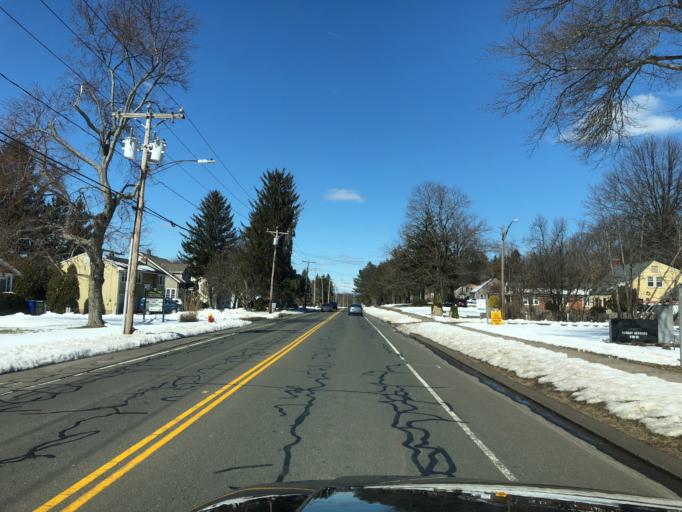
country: US
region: Connecticut
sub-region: Hartford County
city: Newington
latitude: 41.6906
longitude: -72.7445
